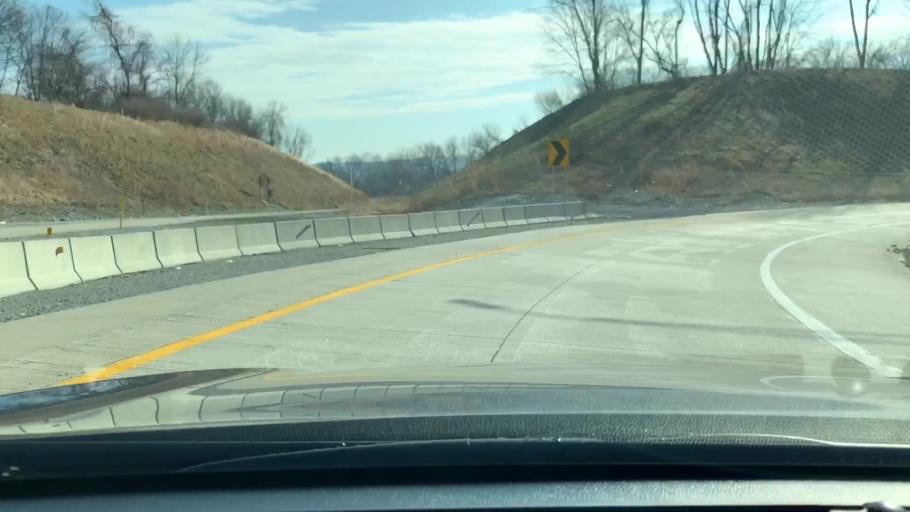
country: US
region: Pennsylvania
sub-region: Chester County
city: Malvern
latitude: 40.0754
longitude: -75.5269
